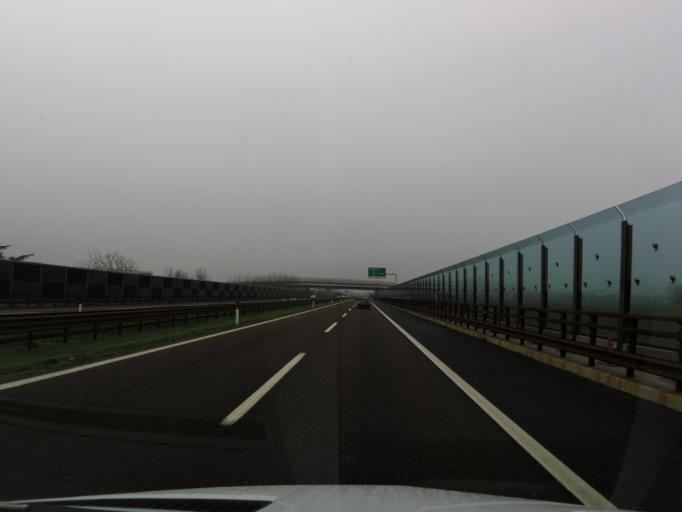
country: IT
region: Emilia-Romagna
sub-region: Provincia di Modena
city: Santa Croce Scuole
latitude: 44.7548
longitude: 10.8443
